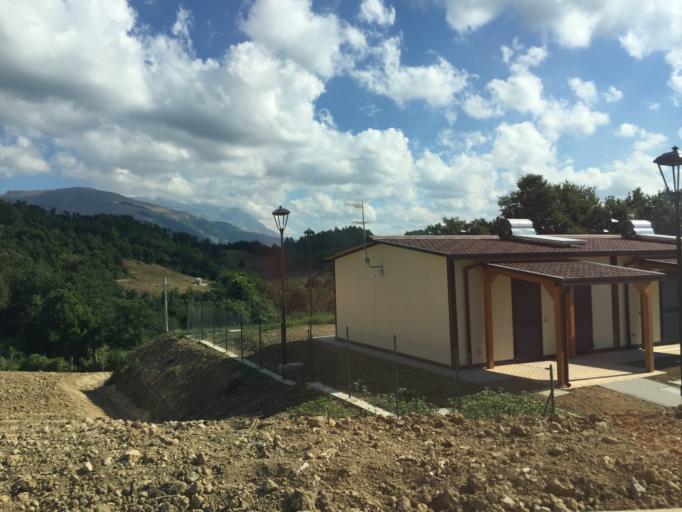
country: IT
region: Latium
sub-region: Provincia di Rieti
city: Accumoli
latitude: 42.6965
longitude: 13.2435
